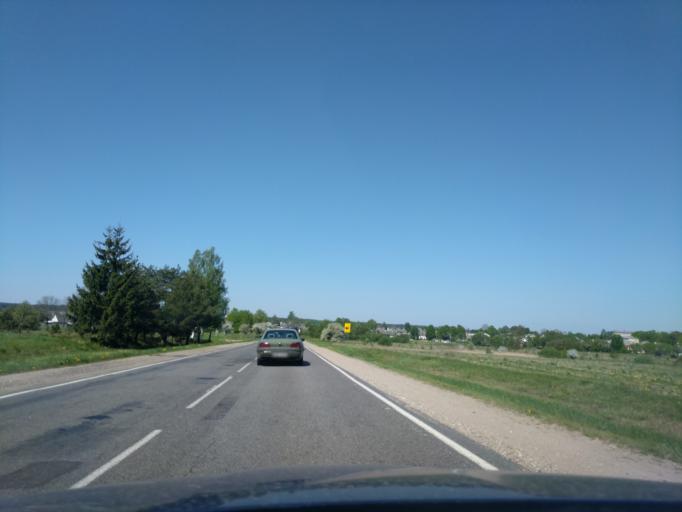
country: BY
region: Minsk
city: Il'ya
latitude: 54.4108
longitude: 27.3033
